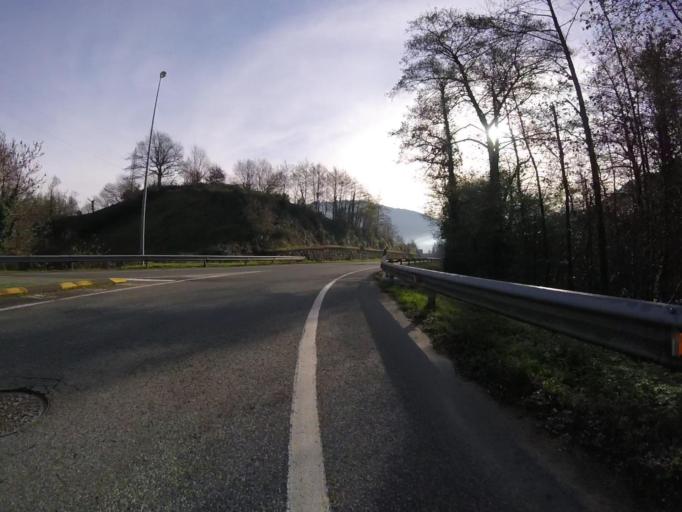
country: ES
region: Navarre
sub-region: Provincia de Navarra
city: Leitza
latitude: 43.0860
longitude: -1.9216
